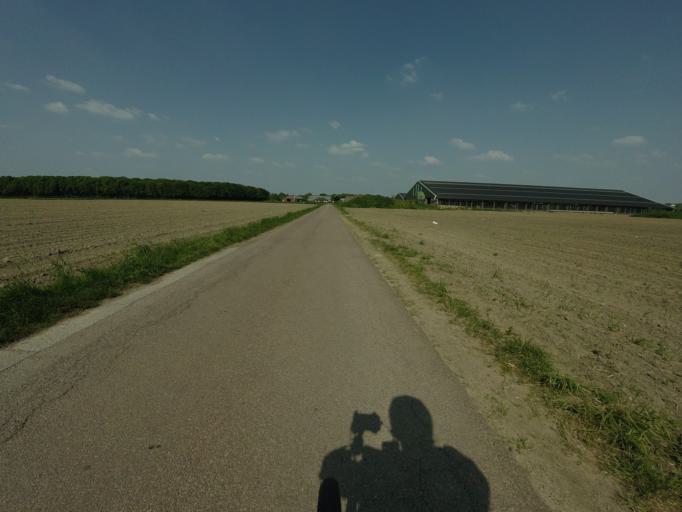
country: BE
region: Flanders
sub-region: Provincie Antwerpen
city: Borsbeek
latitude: 51.1803
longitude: 4.4776
